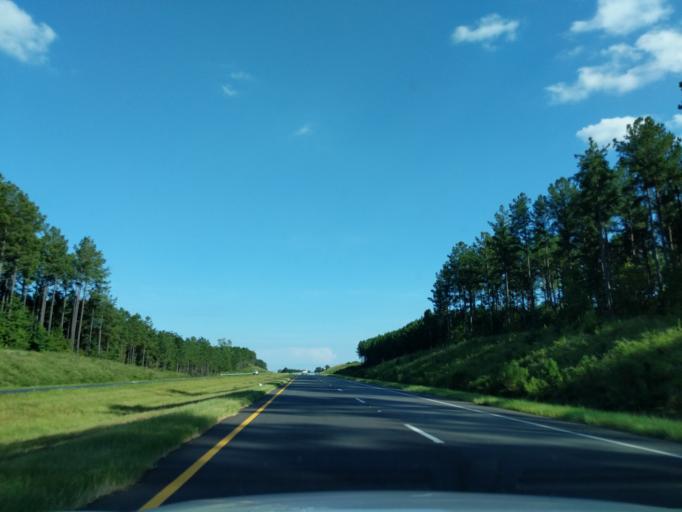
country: US
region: Georgia
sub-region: Wilkes County
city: Washington
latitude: 33.6896
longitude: -82.6461
